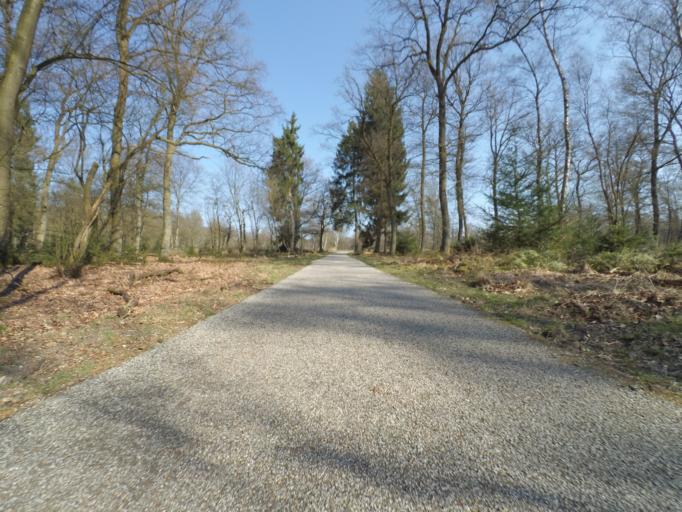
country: NL
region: Gelderland
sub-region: Gemeente Ede
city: Otterlo
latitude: 52.1079
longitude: 5.8415
